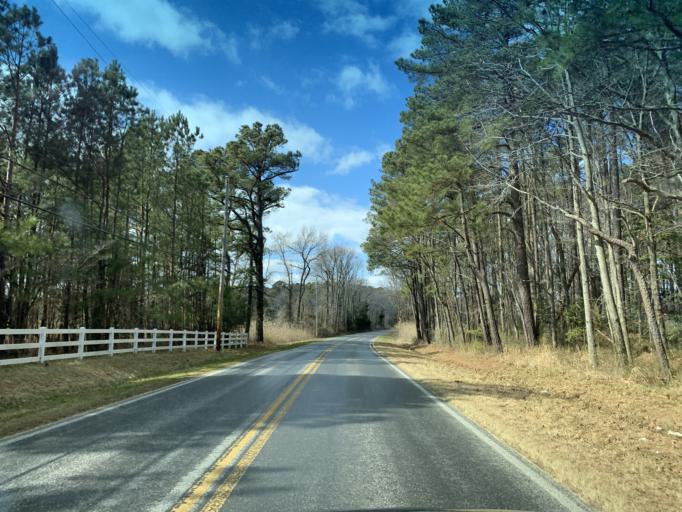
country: US
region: Maryland
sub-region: Queen Anne's County
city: Chester
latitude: 38.9449
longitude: -76.2686
